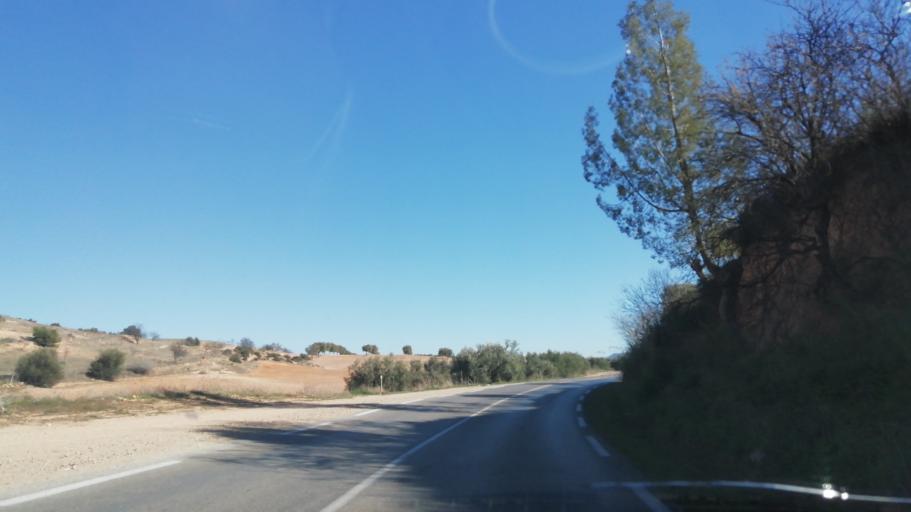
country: DZ
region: Tlemcen
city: Beni Mester
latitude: 34.8264
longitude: -1.5749
